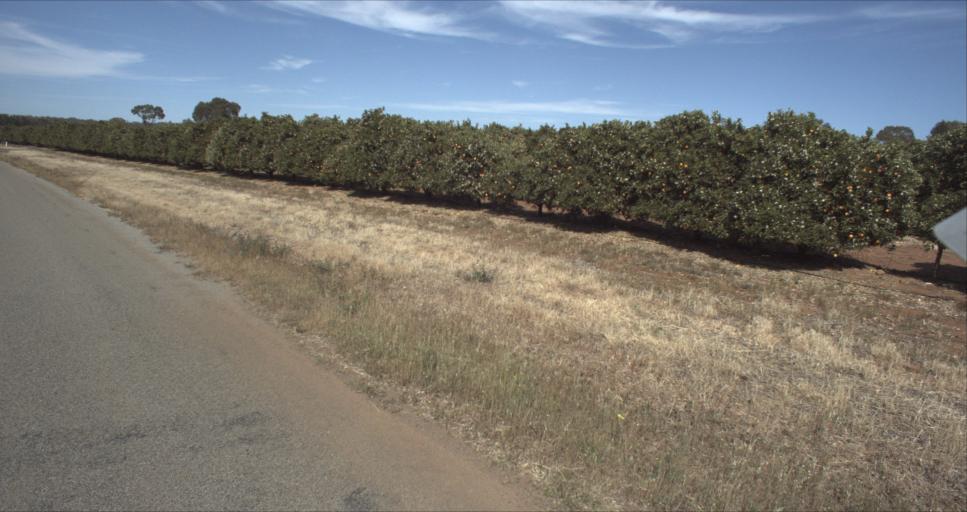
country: AU
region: New South Wales
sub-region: Leeton
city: Leeton
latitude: -34.5862
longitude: 146.4613
